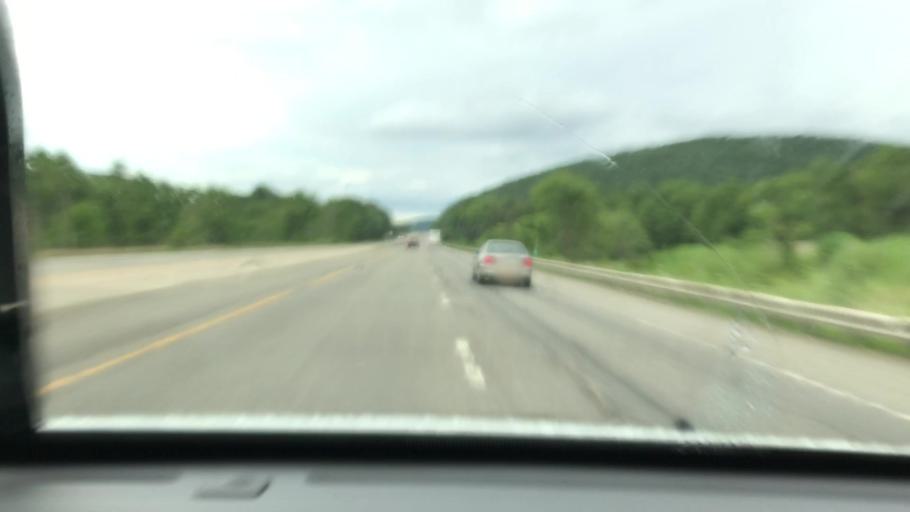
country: US
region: Pennsylvania
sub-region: McKean County
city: Foster Brook
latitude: 42.0444
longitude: -78.6339
